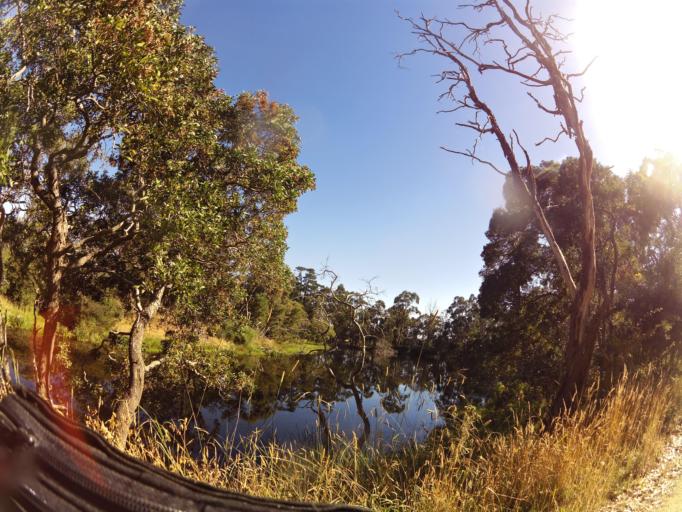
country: AU
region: Victoria
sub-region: Ballarat North
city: Delacombe
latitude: -37.6822
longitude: 143.4285
